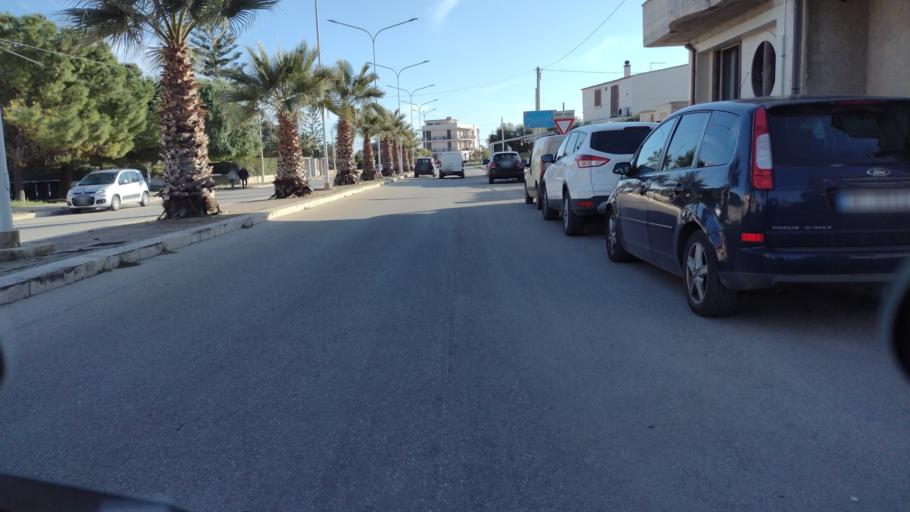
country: IT
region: Sicily
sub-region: Provincia di Siracusa
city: Avola
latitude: 36.9022
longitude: 15.1423
